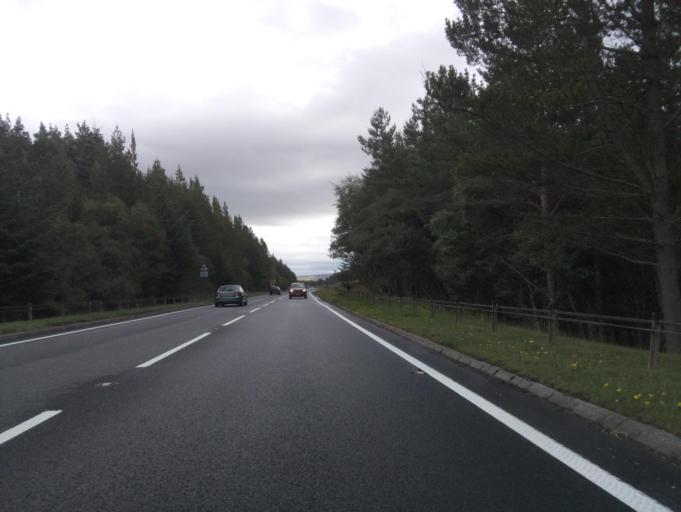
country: GB
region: Scotland
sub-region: Highland
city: Inverness
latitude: 57.3822
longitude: -4.0576
